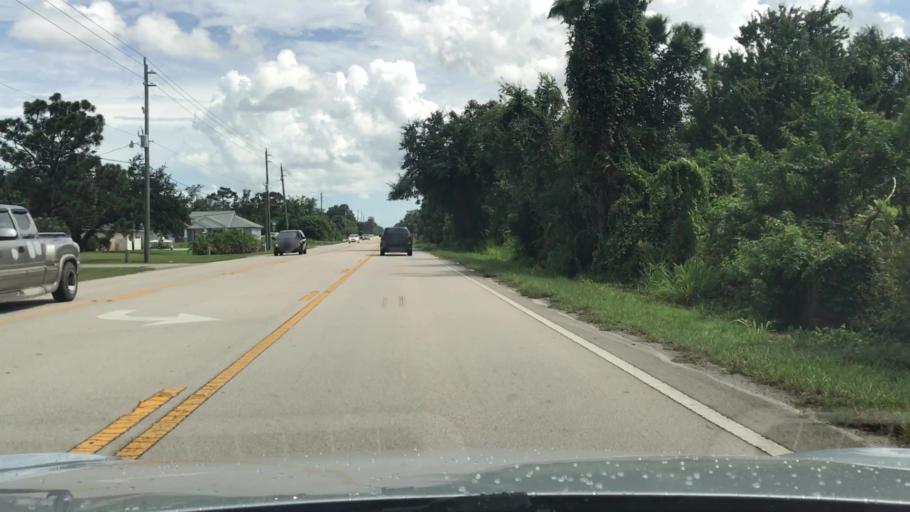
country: US
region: Florida
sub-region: Indian River County
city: Sebastian
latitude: 27.7971
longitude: -80.5010
